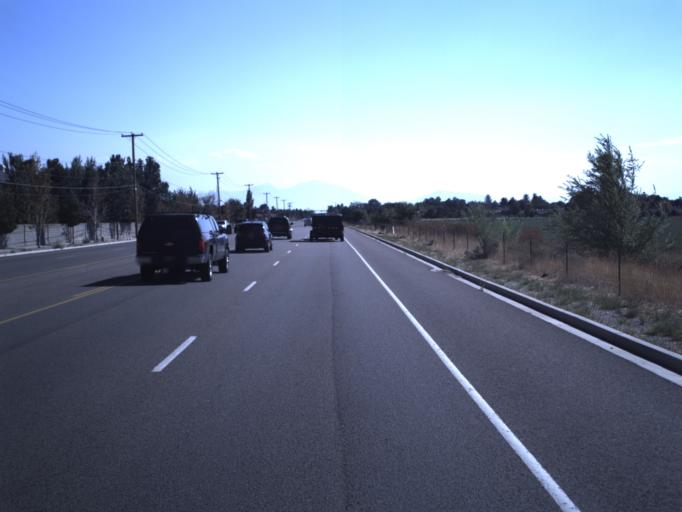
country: US
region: Utah
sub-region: Utah County
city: Cedar Hills
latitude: 40.4048
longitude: -111.7735
